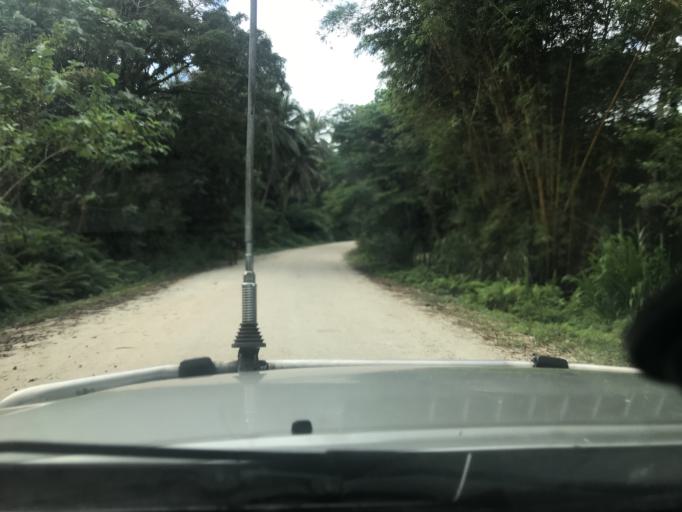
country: SB
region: Malaita
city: Auki
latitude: -8.7830
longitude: 160.7087
